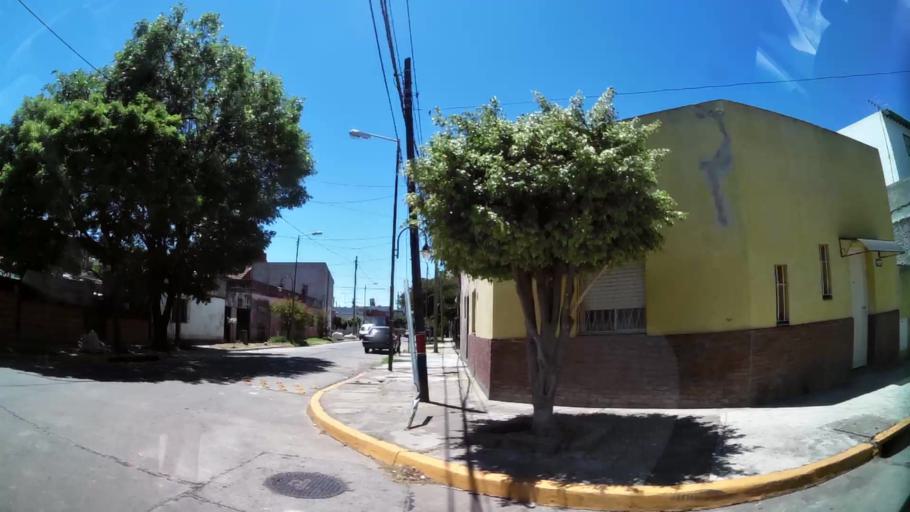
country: AR
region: Buenos Aires
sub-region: Partido de Tigre
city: Tigre
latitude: -34.4542
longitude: -58.5550
